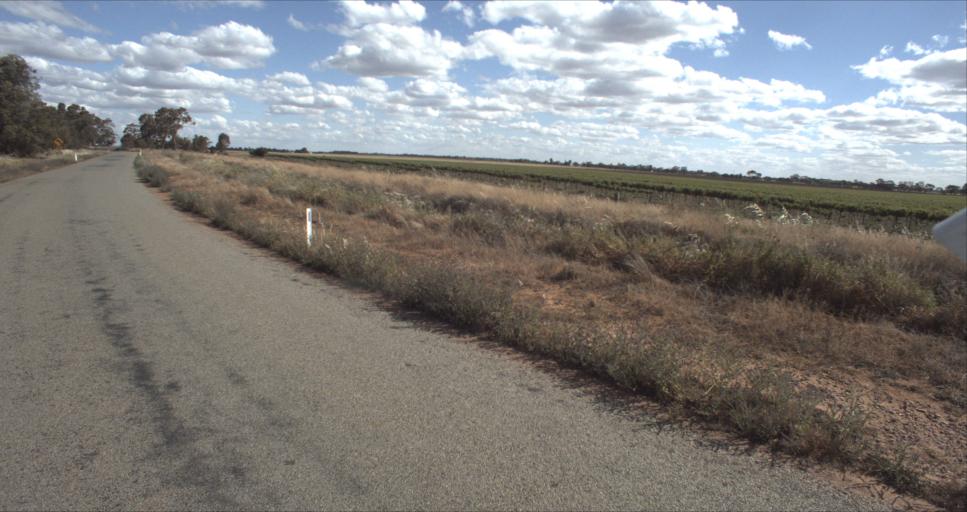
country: AU
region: New South Wales
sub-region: Griffith
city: Griffith
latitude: -34.4044
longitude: 146.2154
